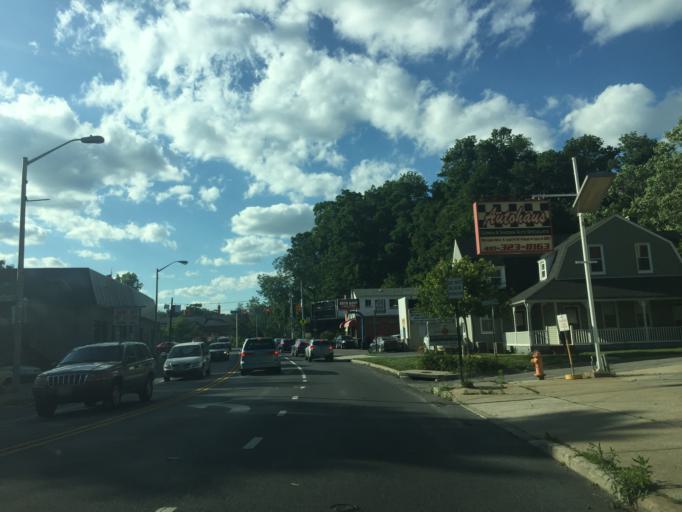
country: US
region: Maryland
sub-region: Baltimore County
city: Towson
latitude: 39.3664
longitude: -76.6478
